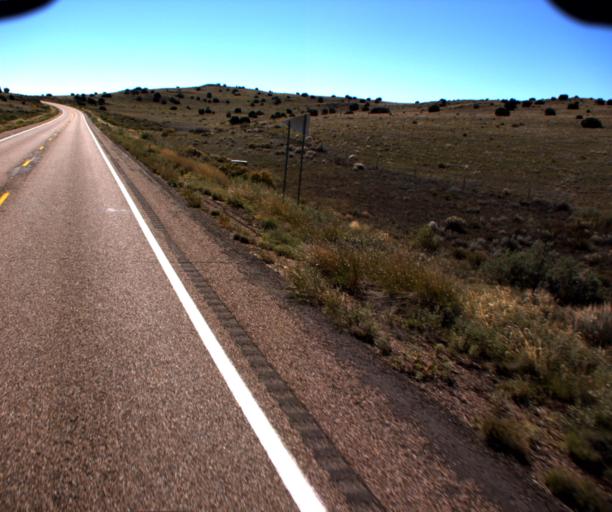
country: US
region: Arizona
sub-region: Apache County
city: Saint Johns
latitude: 34.5646
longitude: -109.5071
